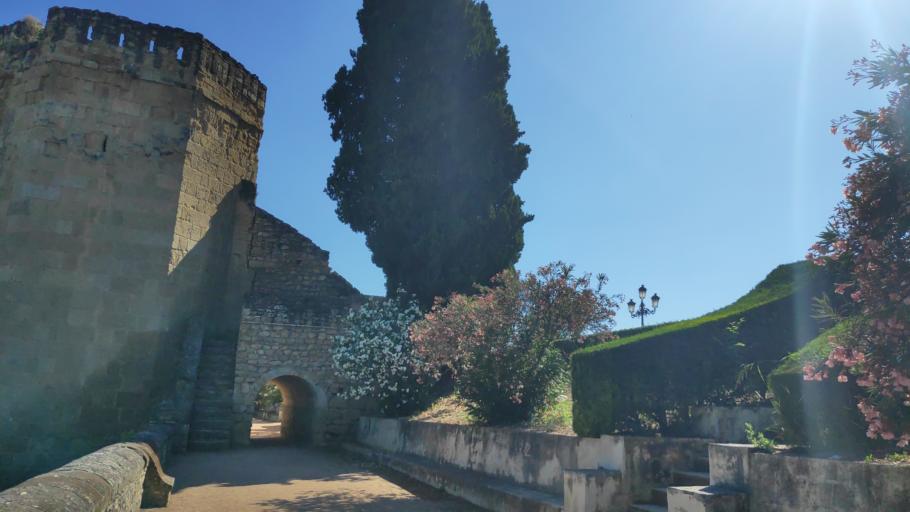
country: ES
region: Andalusia
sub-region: Province of Cordoba
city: Cordoba
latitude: 37.8742
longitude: -4.7827
